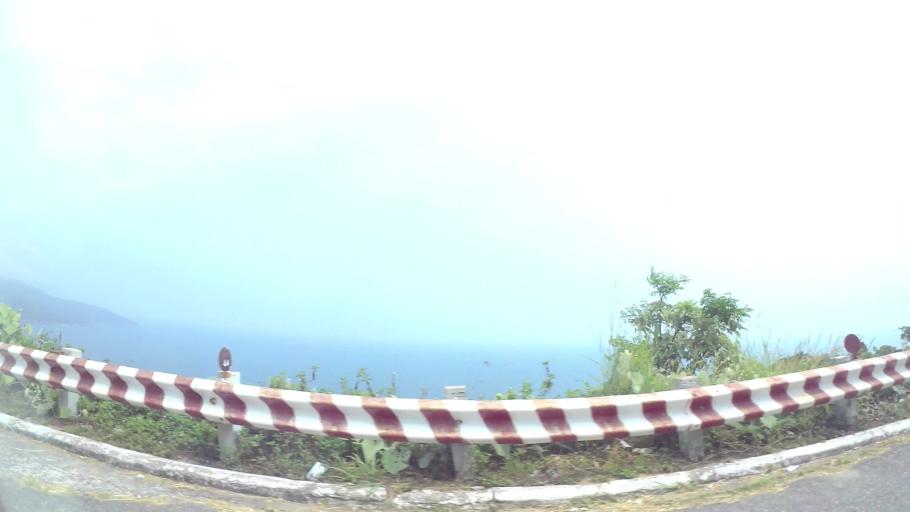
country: VN
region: Da Nang
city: Son Tra
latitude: 16.1010
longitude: 108.3079
